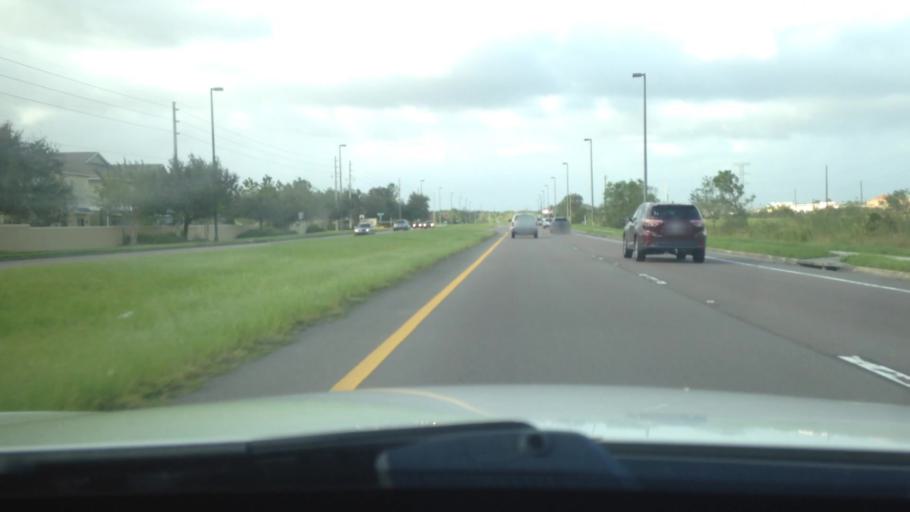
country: US
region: Florida
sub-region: Orange County
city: Conway
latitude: 28.4683
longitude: -81.2899
